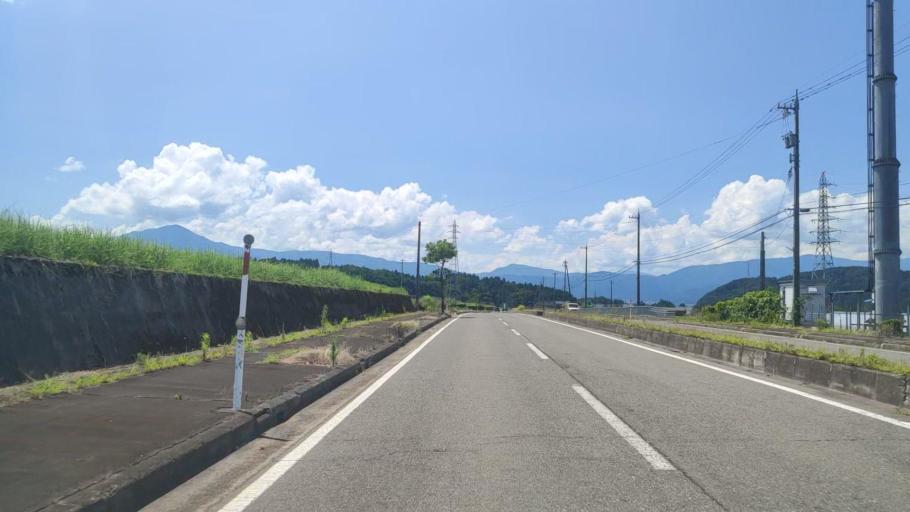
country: JP
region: Fukui
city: Katsuyama
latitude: 36.0381
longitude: 136.5197
